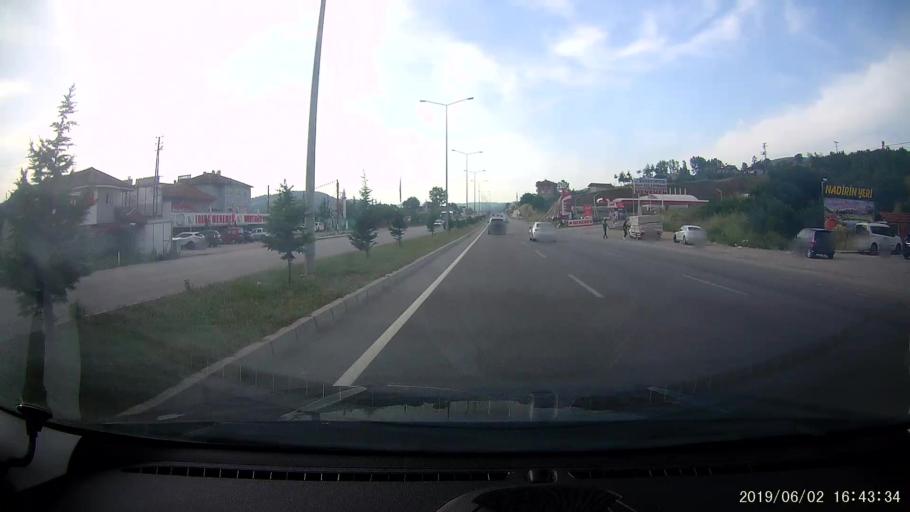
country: TR
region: Samsun
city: Kavak
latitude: 41.1374
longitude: 36.1256
